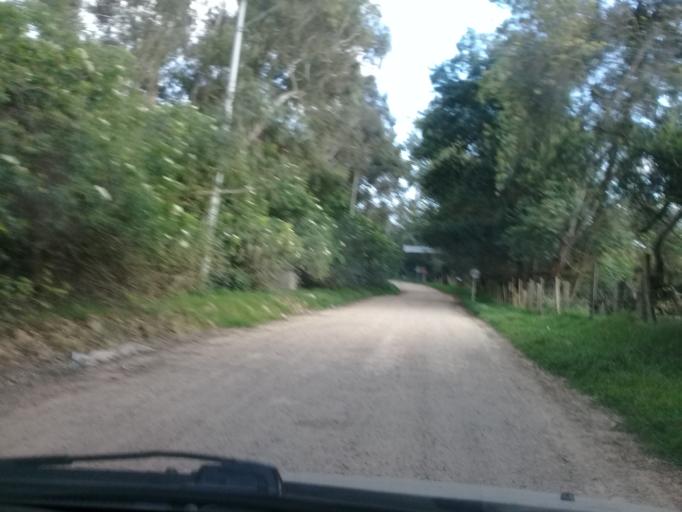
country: CO
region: Cundinamarca
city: Madrid
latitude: 4.7853
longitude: -74.2724
